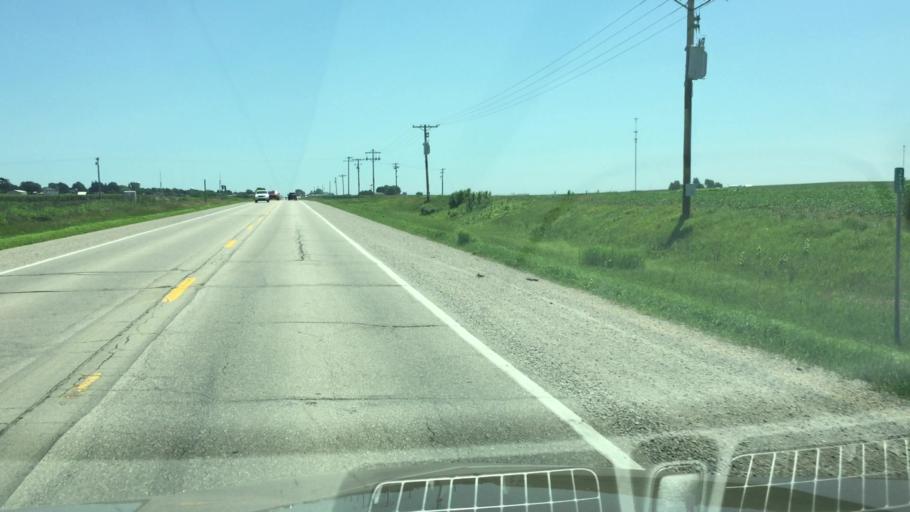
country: US
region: Iowa
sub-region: Cedar County
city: Mechanicsville
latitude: 41.9091
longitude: -91.2817
